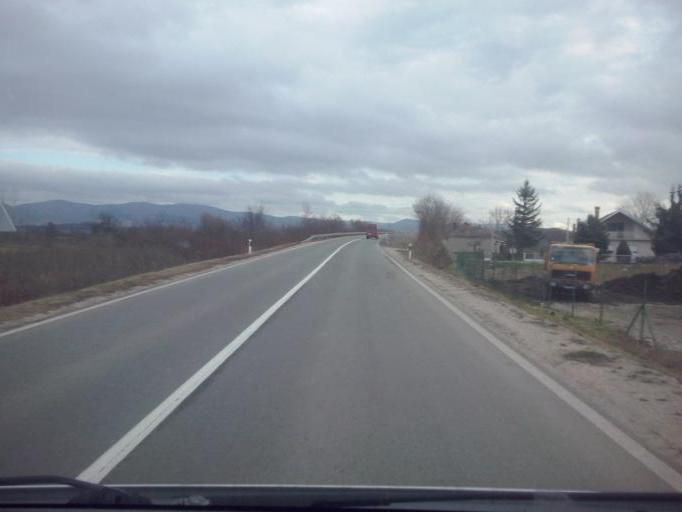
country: RS
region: Central Serbia
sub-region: Pomoravski Okrug
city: Paracin
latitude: 43.8681
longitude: 21.4764
